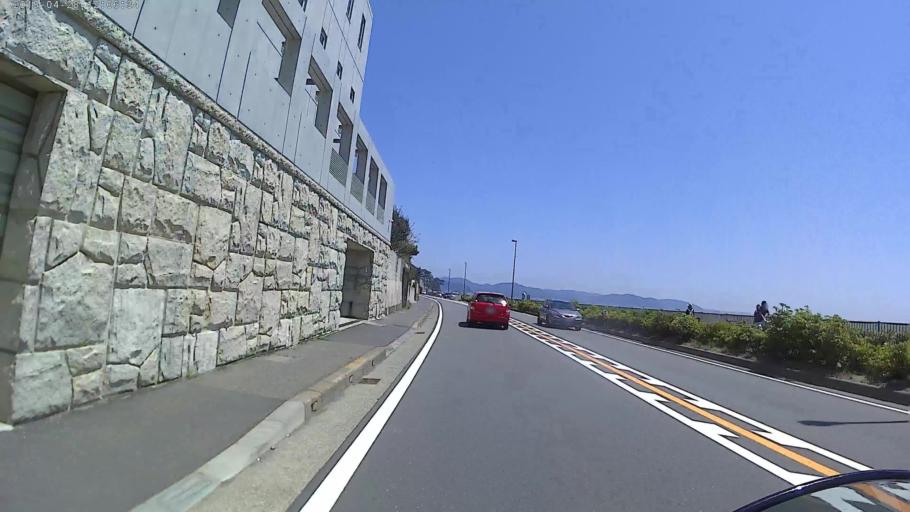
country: JP
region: Kanagawa
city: Kamakura
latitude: 35.3040
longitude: 139.5157
